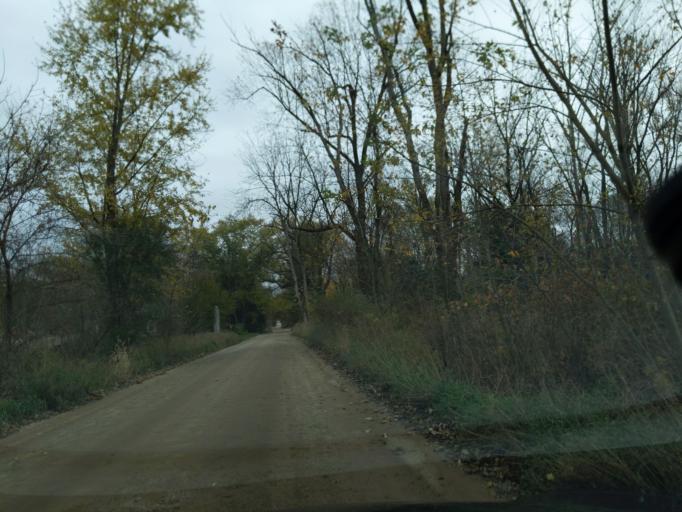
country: US
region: Michigan
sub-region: Eaton County
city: Eaton Rapids
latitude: 42.5529
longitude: -84.6155
